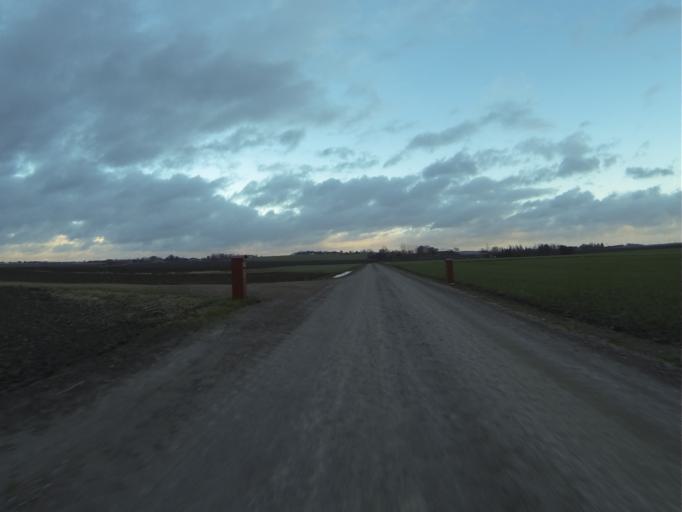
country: SE
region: Skane
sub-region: Lunds Kommun
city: Genarp
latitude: 55.6420
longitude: 13.3296
